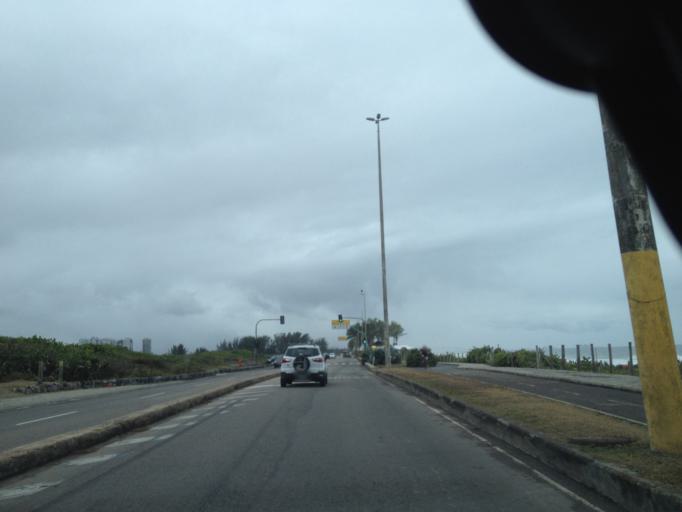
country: BR
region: Rio de Janeiro
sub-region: Nilopolis
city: Nilopolis
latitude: -23.0208
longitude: -43.4407
